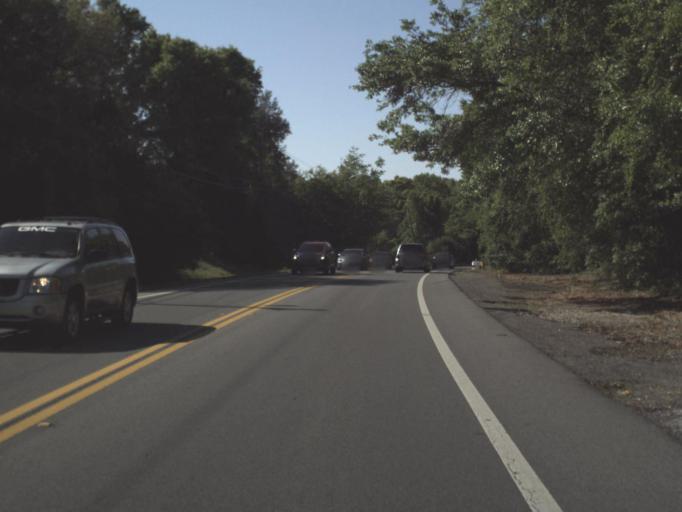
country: US
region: Florida
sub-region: Escambia County
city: Ferry Pass
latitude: 30.4950
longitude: -87.1588
